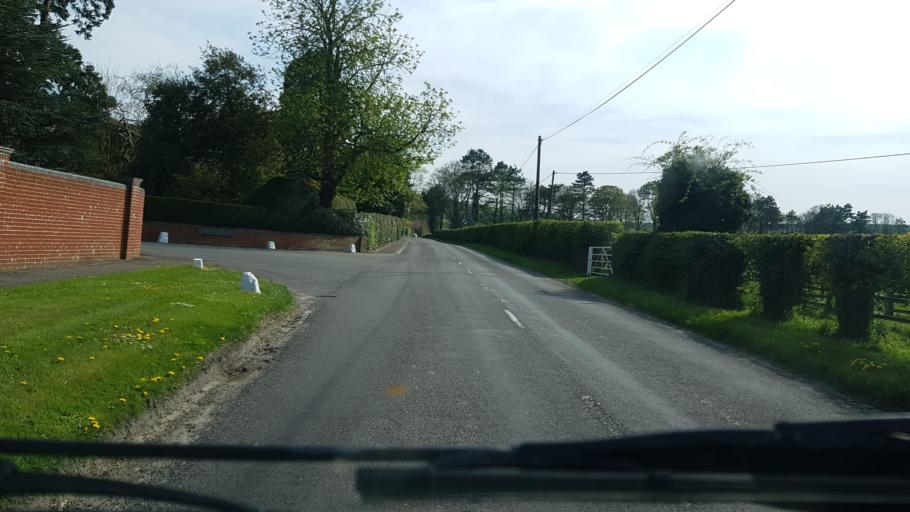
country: GB
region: England
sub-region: Hampshire
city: Kingsclere
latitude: 51.3163
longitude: -1.2530
